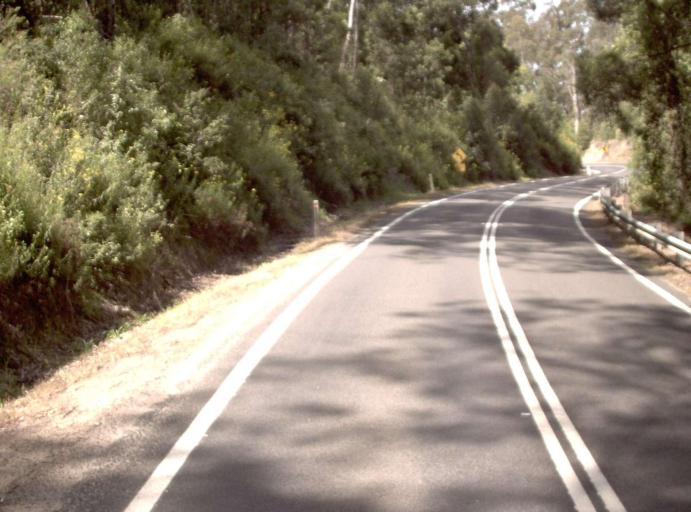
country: AU
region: New South Wales
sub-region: Bombala
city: Bombala
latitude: -37.5547
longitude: 149.3570
